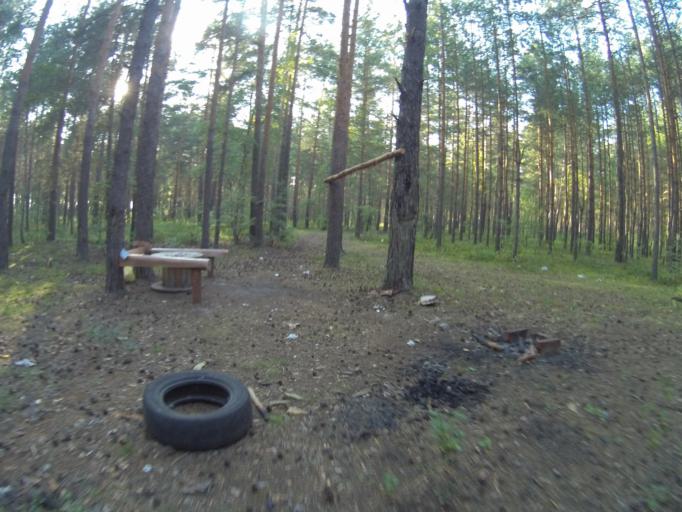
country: RU
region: Vladimir
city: Kommunar
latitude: 56.1178
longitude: 40.4641
